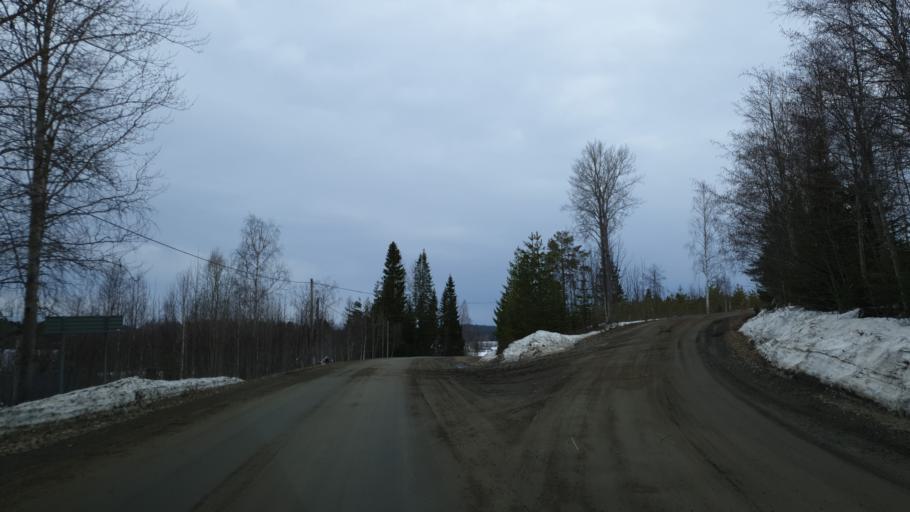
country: SE
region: Vaesterbotten
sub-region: Skelleftea Kommun
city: Burea
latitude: 64.3223
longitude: 21.1385
